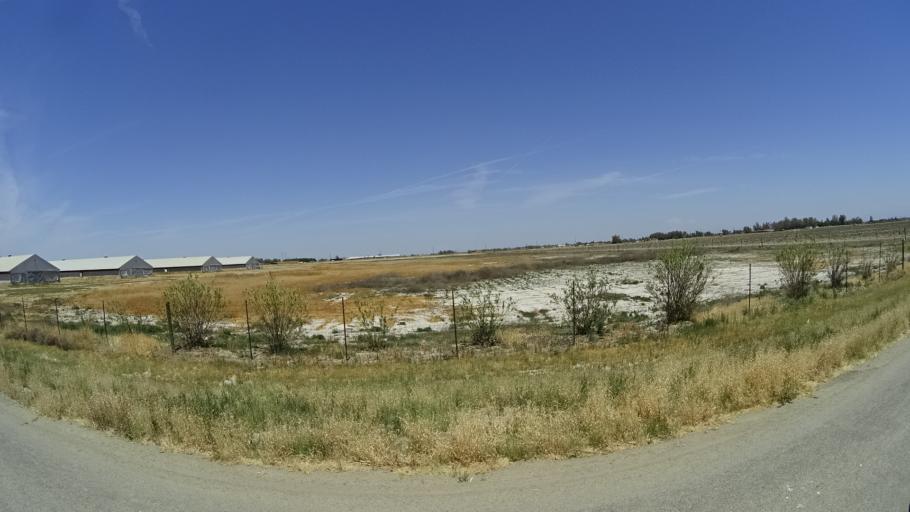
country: US
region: California
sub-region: Kings County
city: Stratford
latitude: 36.2331
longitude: -119.7947
